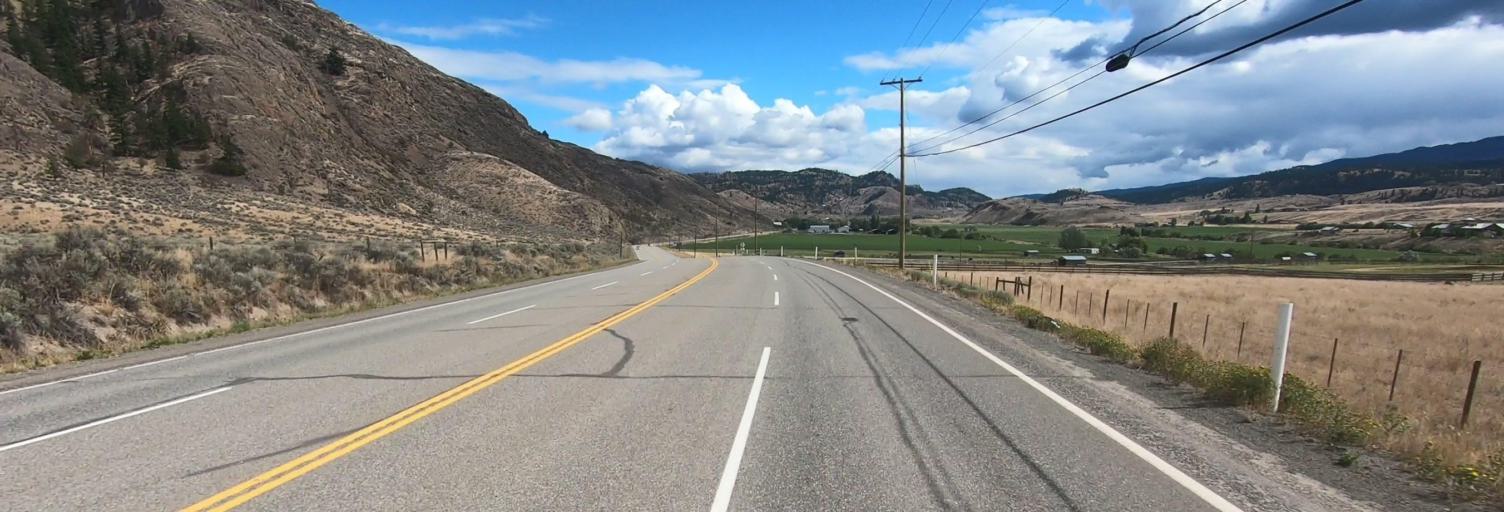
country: CA
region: British Columbia
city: Logan Lake
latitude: 50.7117
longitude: -120.6203
